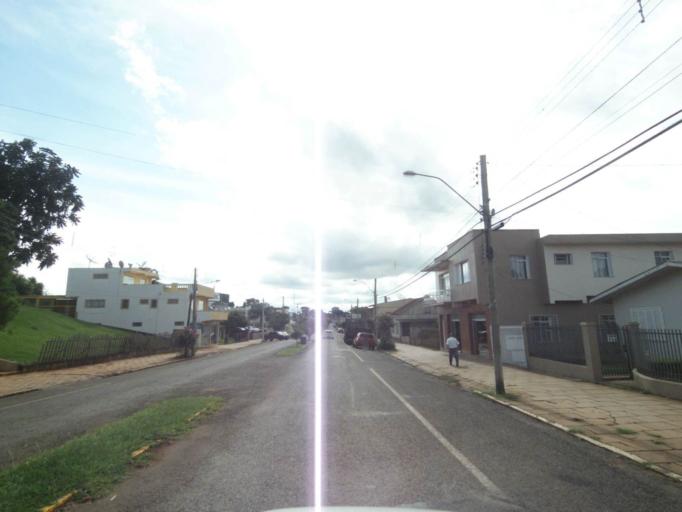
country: BR
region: Rio Grande do Sul
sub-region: Lagoa Vermelha
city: Lagoa Vermelha
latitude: -28.2095
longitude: -51.5315
